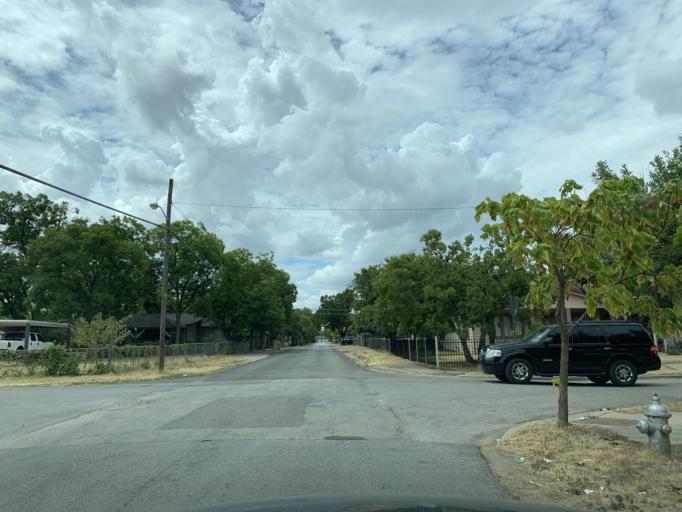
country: US
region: Texas
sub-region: Dallas County
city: Cockrell Hill
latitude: 32.7481
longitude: -96.8753
